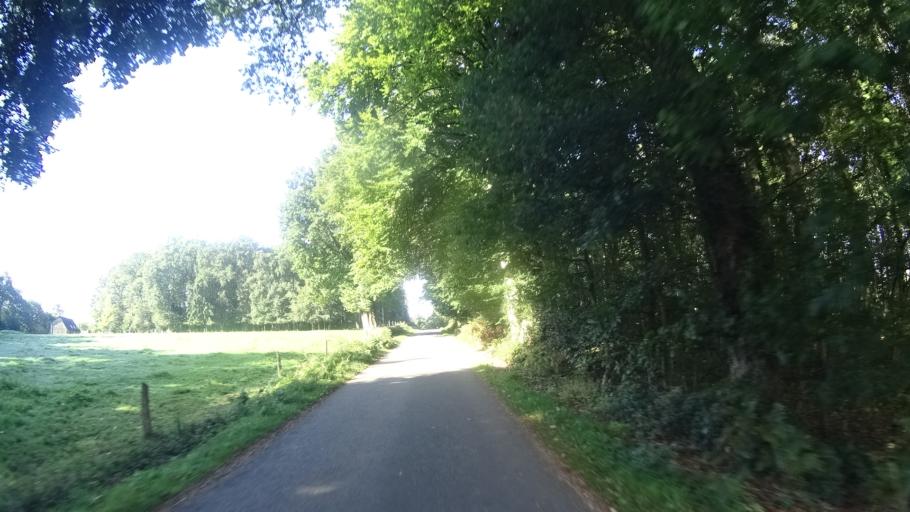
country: FR
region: Brittany
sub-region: Departement du Morbihan
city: Peillac
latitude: 47.7399
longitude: -2.2214
